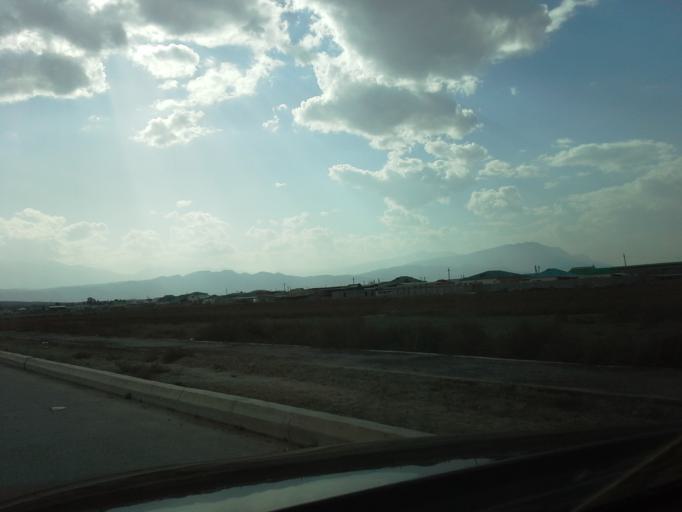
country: TM
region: Ahal
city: Ashgabat
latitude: 37.9900
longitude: 58.2995
